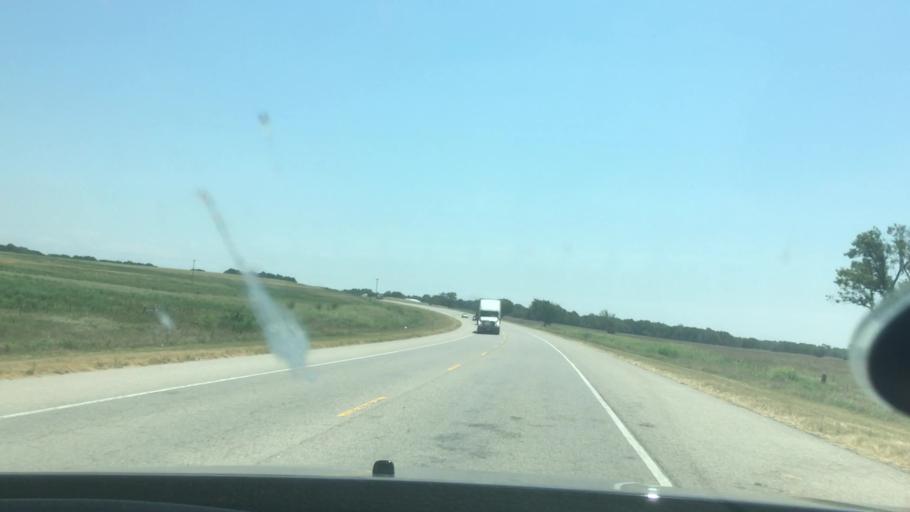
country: US
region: Oklahoma
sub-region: Pontotoc County
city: Ada
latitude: 34.6865
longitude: -96.5929
